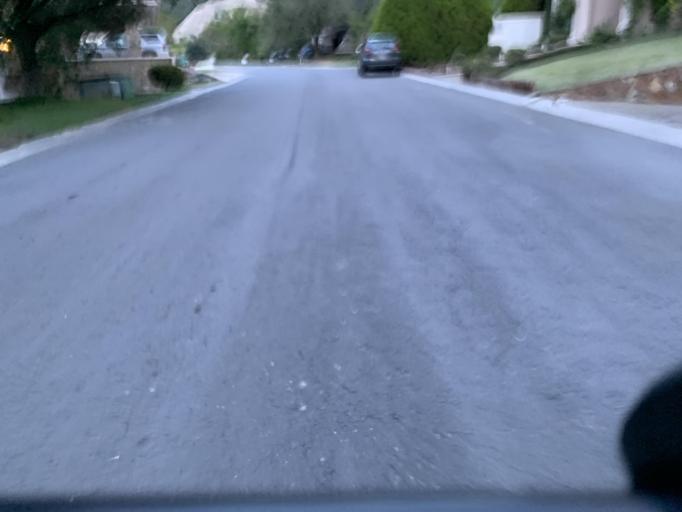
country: MX
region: Nuevo Leon
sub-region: Juarez
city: Bosques de San Pedro
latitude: 25.5150
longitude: -100.1876
